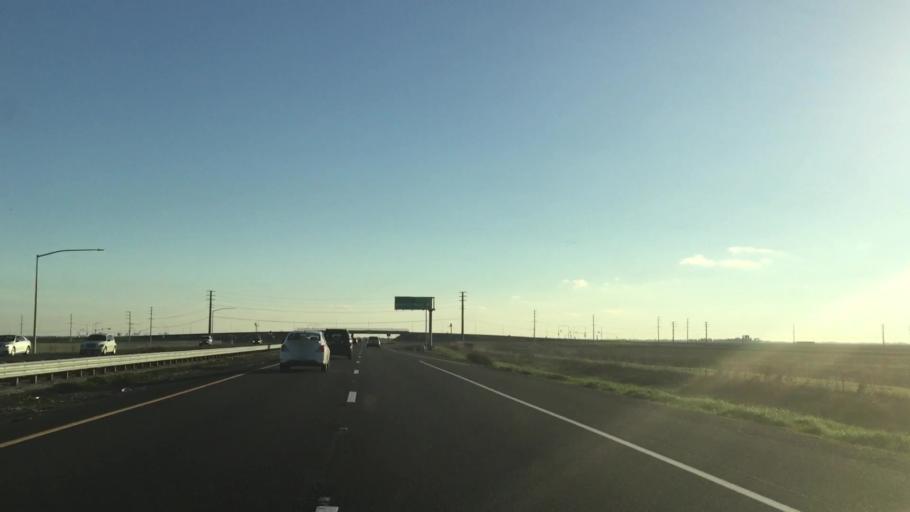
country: US
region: California
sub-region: Sacramento County
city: Elverta
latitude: 38.7213
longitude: -121.5405
